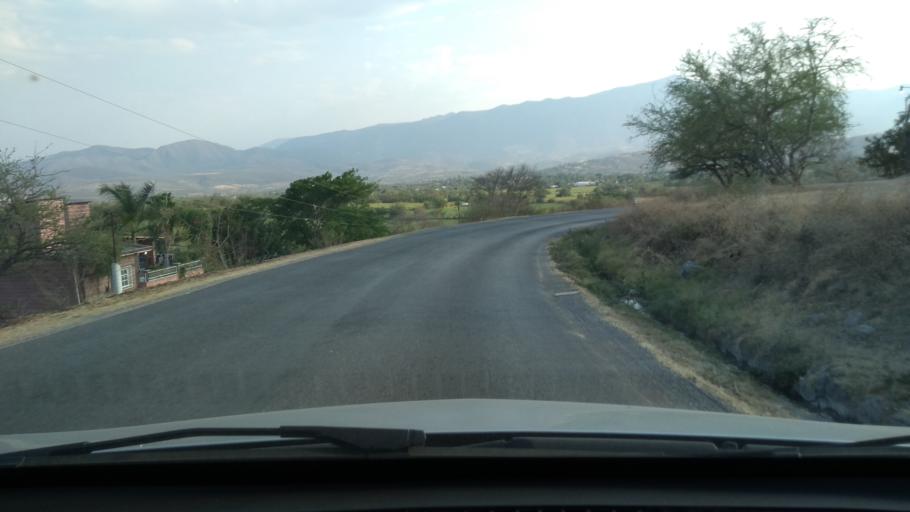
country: MX
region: Morelos
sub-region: Jojutla
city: Tehuixtla
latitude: 18.5724
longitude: -99.2640
